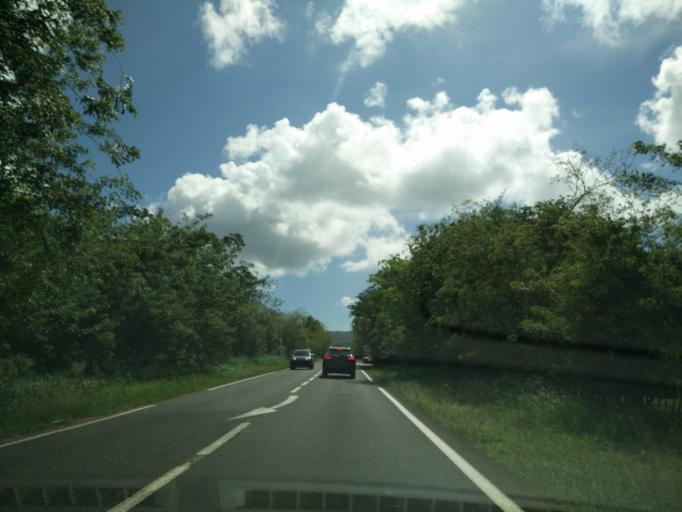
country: MQ
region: Martinique
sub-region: Martinique
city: Les Trois-Ilets
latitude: 14.5292
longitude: -61.0148
